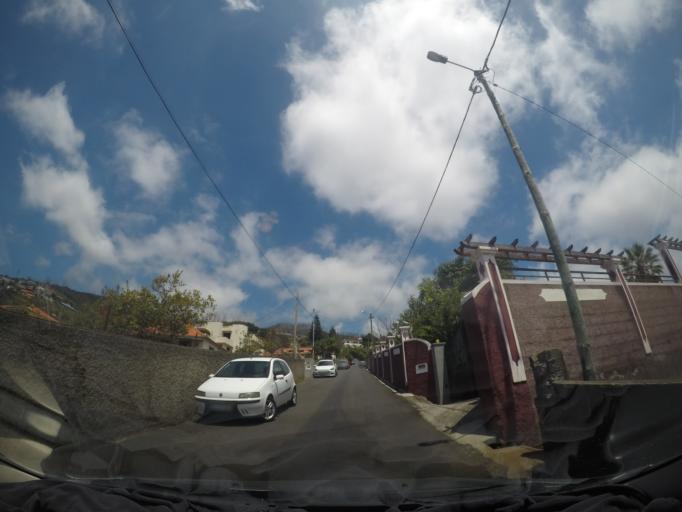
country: PT
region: Madeira
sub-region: Funchal
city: Nossa Senhora do Monte
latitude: 32.6728
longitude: -16.9253
